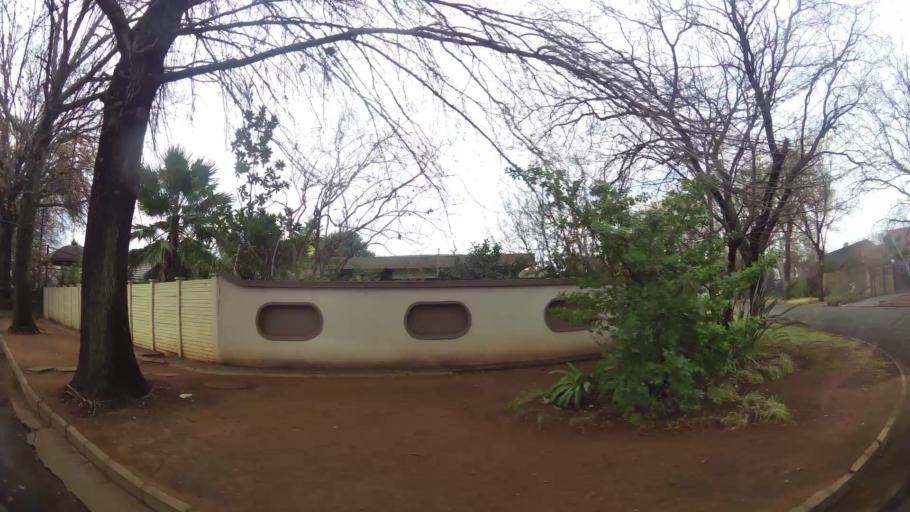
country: ZA
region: Gauteng
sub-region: Sedibeng District Municipality
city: Vereeniging
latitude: -26.6430
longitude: 27.9741
